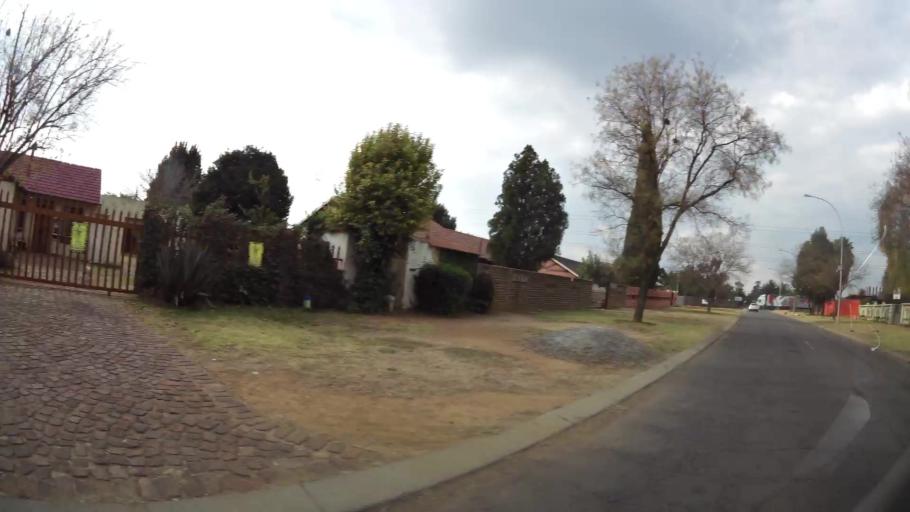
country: ZA
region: Gauteng
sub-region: Ekurhuleni Metropolitan Municipality
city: Benoni
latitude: -26.1156
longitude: 28.3733
